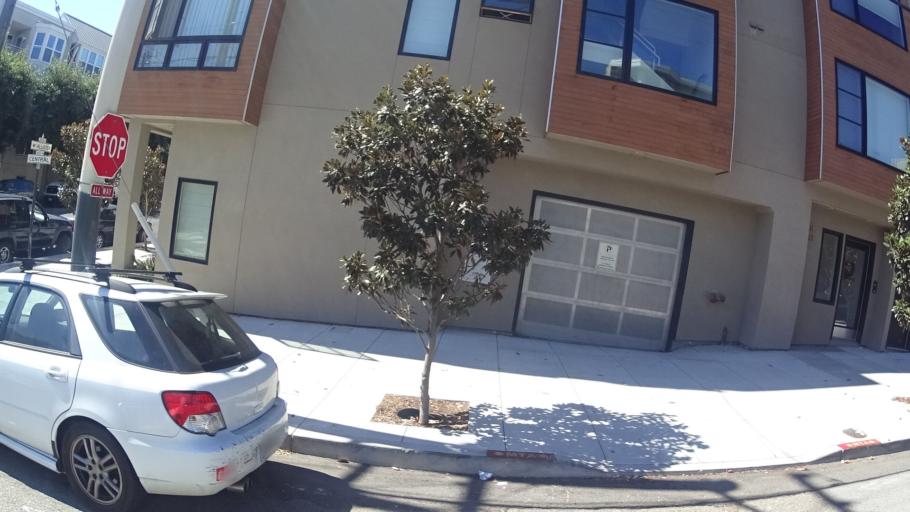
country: US
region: California
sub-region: San Francisco County
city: San Francisco
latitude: 37.7773
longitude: -122.4451
